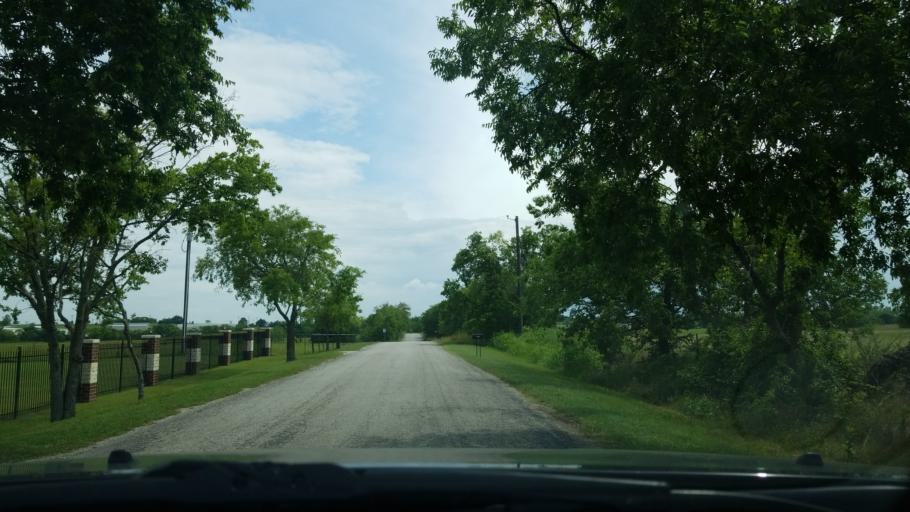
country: US
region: Texas
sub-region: Denton County
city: Sanger
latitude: 33.3060
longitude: -97.1751
